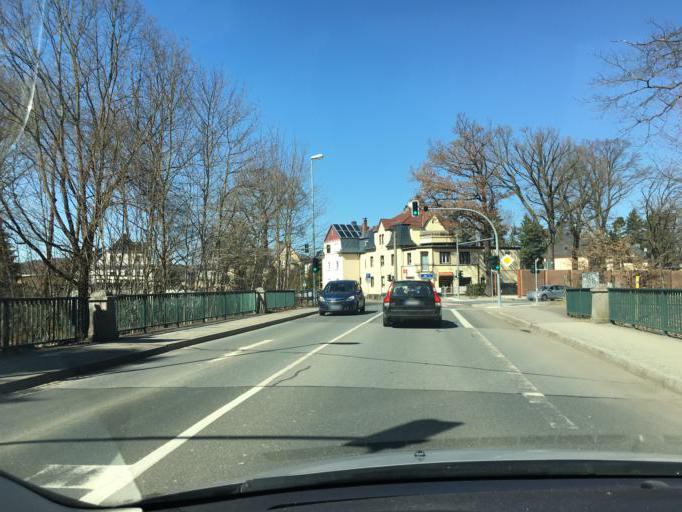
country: DE
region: Saxony
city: Neukirchen
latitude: 50.8230
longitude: 12.8363
